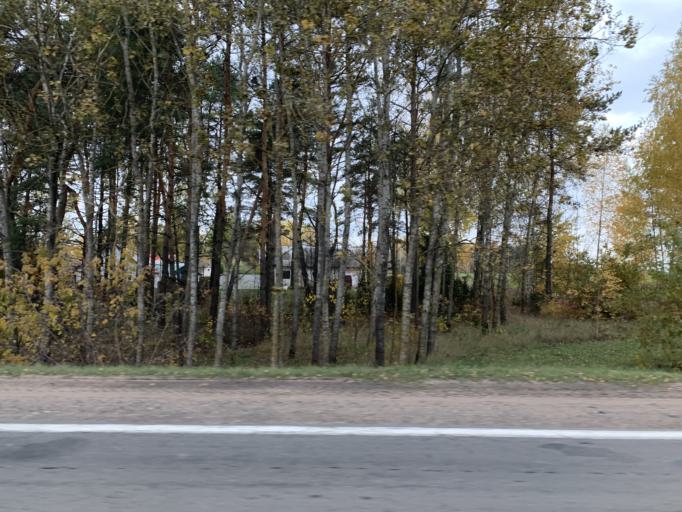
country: BY
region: Minsk
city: Stowbtsy
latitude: 53.5000
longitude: 26.7495
